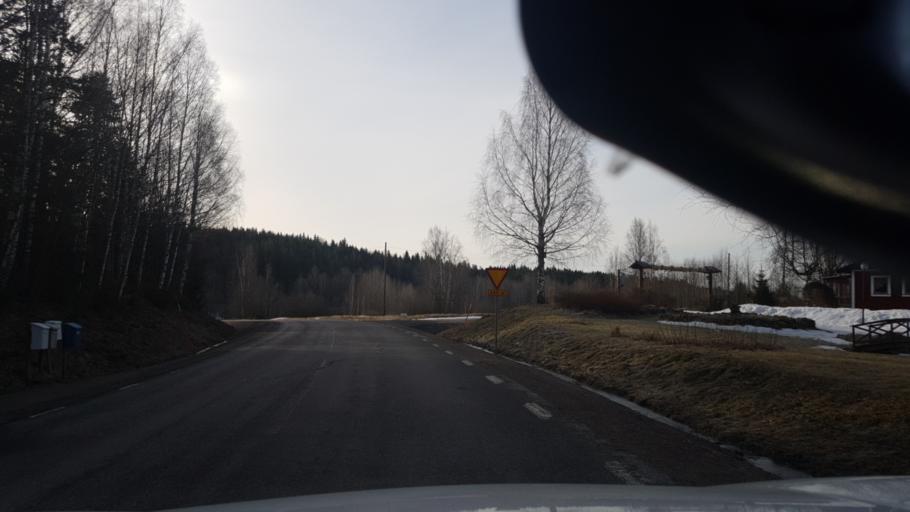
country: SE
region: Vaermland
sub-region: Eda Kommun
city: Amotfors
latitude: 59.8700
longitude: 12.5439
